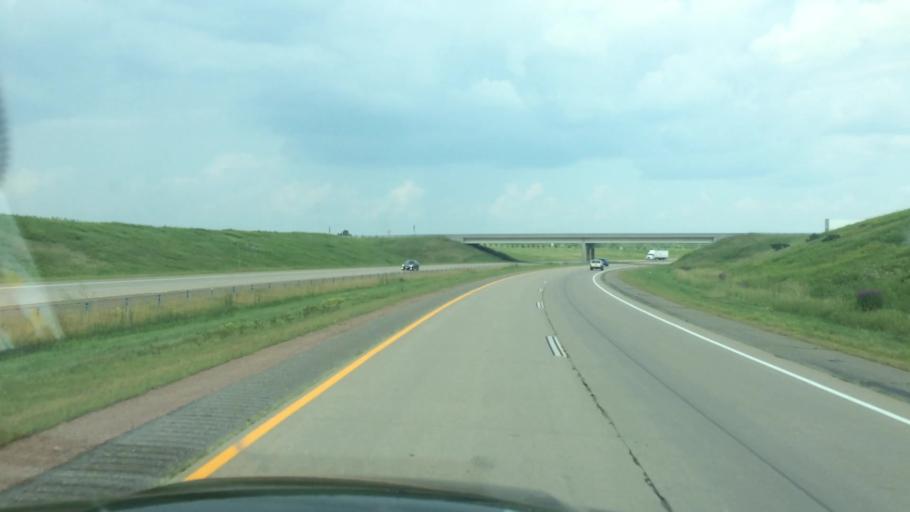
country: US
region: Wisconsin
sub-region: Clark County
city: Abbotsford
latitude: 44.9425
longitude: -90.2918
